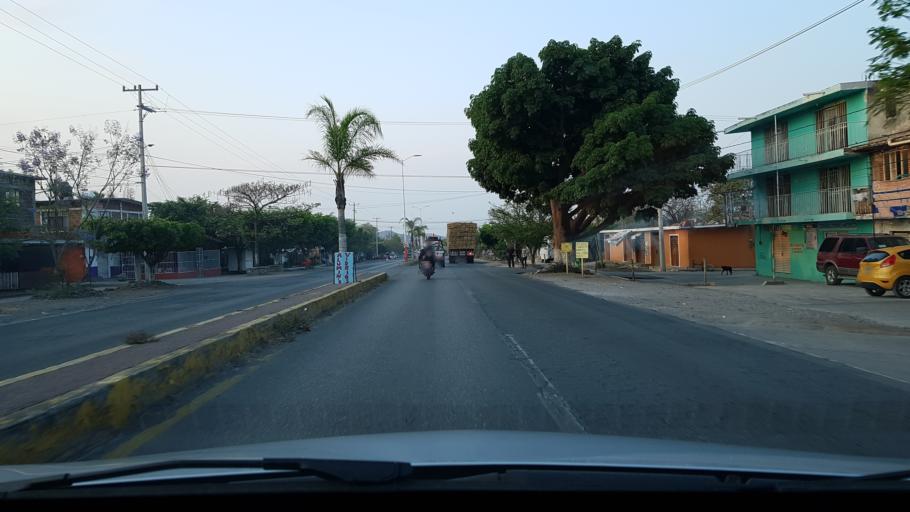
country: MX
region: Morelos
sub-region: Jonacatepec
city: Amacuitlapilco
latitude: 18.6955
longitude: -98.8017
